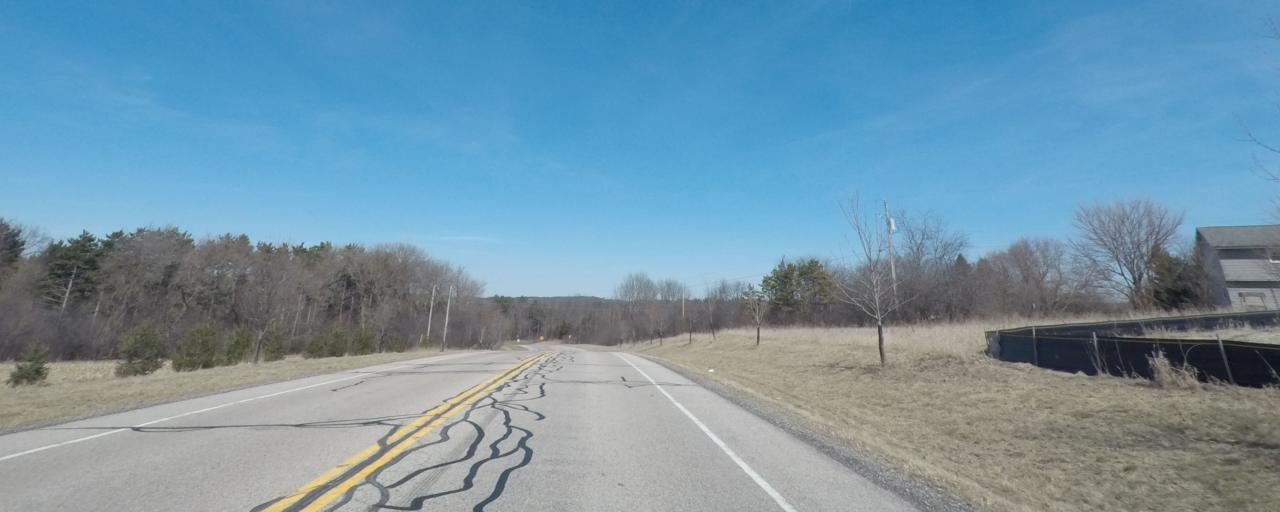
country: US
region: Wisconsin
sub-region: Waukesha County
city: Hartland
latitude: 43.1153
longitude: -88.3562
